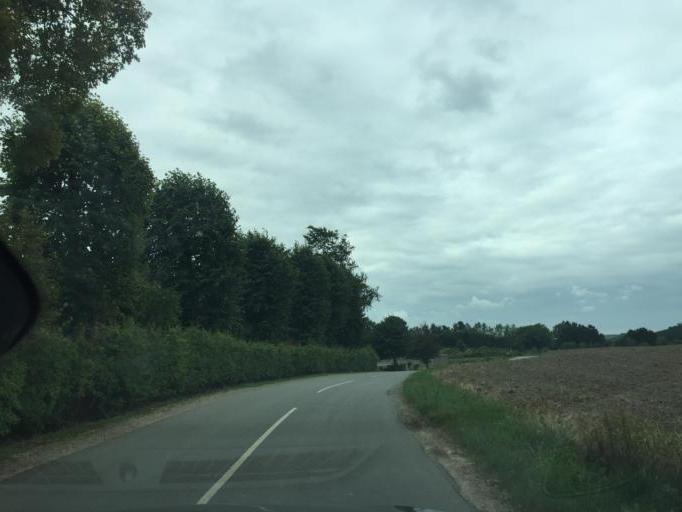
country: DK
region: South Denmark
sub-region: Assens Kommune
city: Tommerup Stationsby
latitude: 55.3816
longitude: 10.1748
